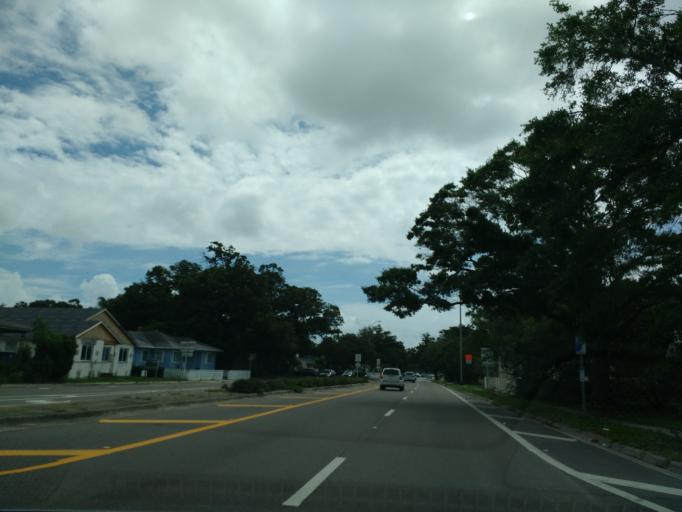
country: US
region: Florida
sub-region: Pinellas County
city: Saint Petersburg
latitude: 27.7919
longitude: -82.6589
